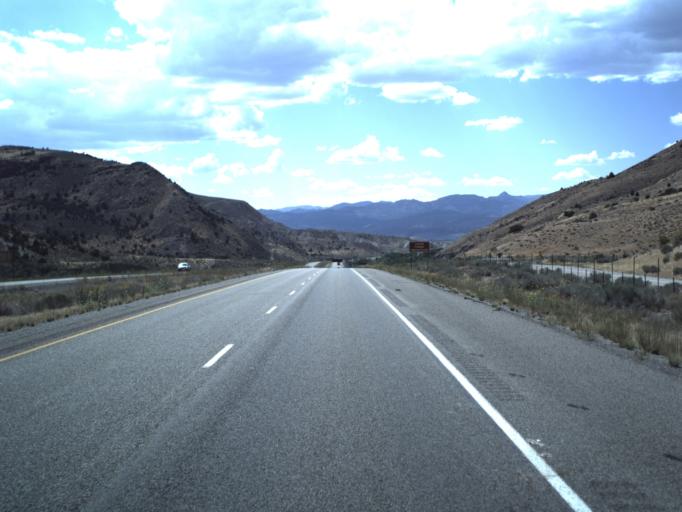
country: US
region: Utah
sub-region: Sevier County
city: Salina
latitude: 38.9325
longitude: -111.8112
